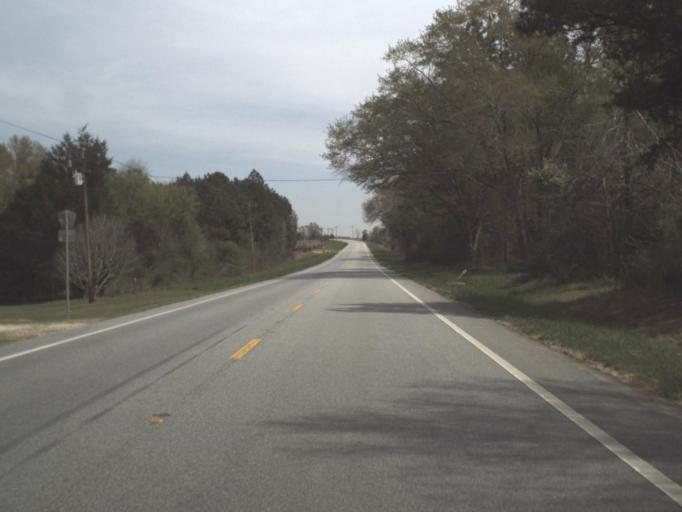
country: US
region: Alabama
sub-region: Geneva County
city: Geneva
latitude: 30.9413
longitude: -85.7919
